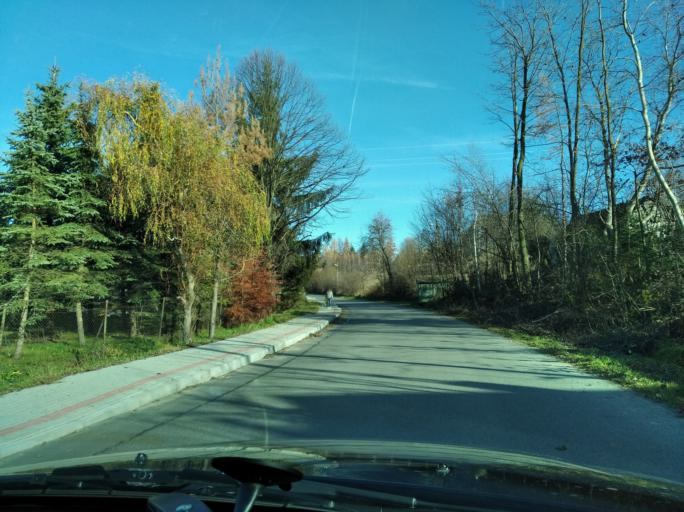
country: PL
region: Subcarpathian Voivodeship
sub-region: Powiat rzeszowski
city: Lutoryz
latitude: 49.9627
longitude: 21.8951
